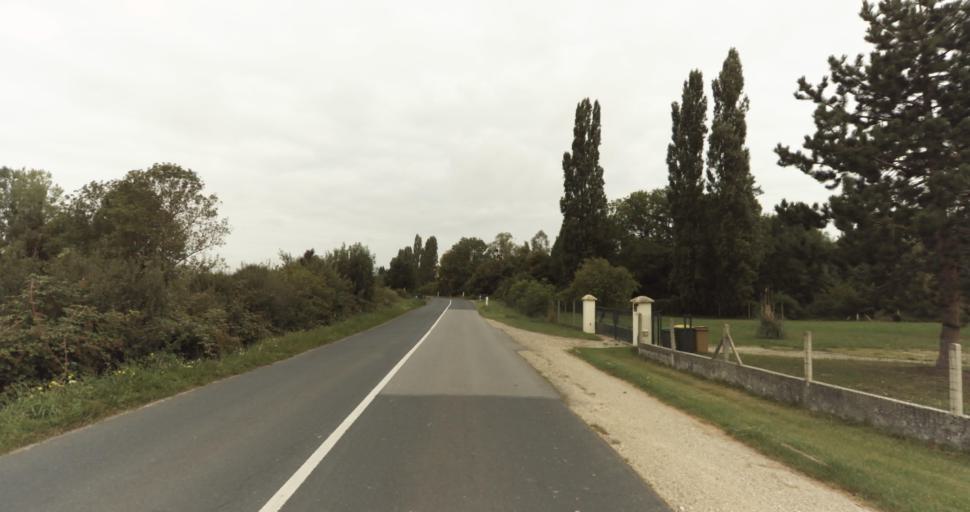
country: FR
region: Haute-Normandie
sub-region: Departement de l'Eure
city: Garennes-sur-Eure
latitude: 48.9159
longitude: 1.4577
